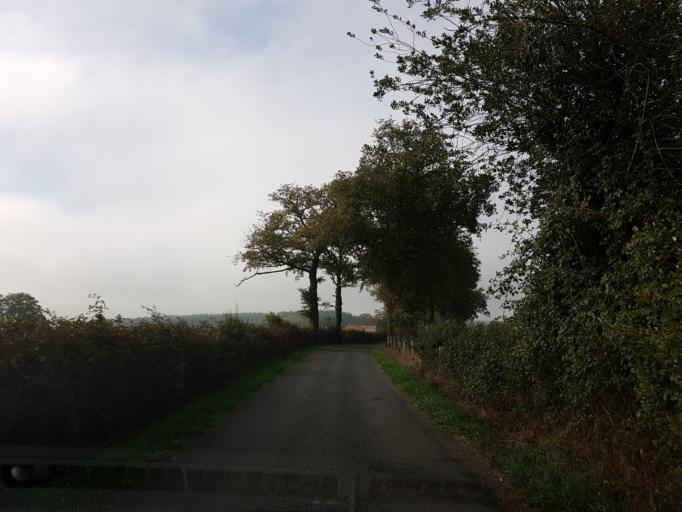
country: FR
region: Poitou-Charentes
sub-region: Departement de la Charente
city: Etagnac
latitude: 45.9109
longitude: 0.7396
